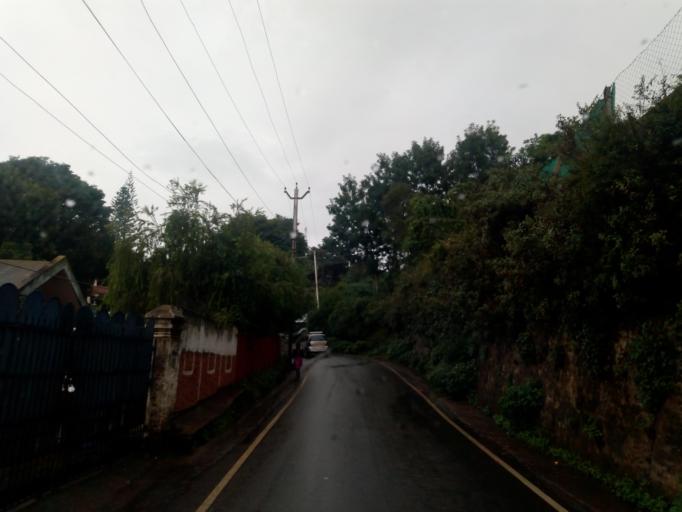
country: IN
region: Tamil Nadu
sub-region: Nilgiri
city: Wellington
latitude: 11.3488
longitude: 76.8030
